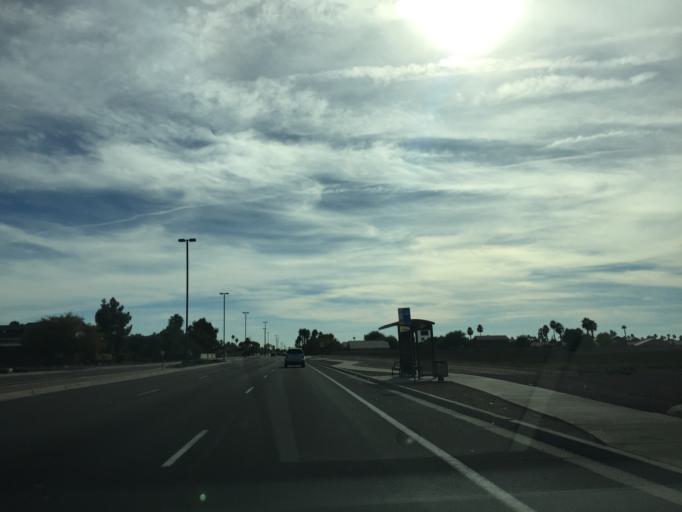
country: US
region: Arizona
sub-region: Maricopa County
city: Gilbert
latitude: 33.3207
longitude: -111.7900
